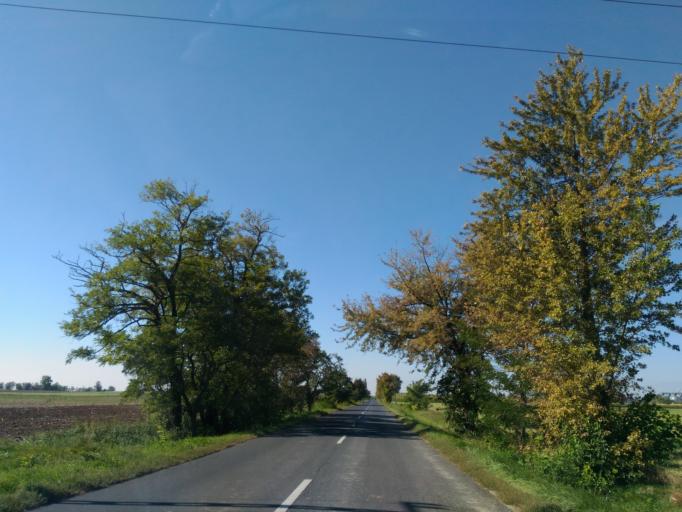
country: HU
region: Fejer
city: Ivancsa
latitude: 47.1783
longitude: 18.8210
